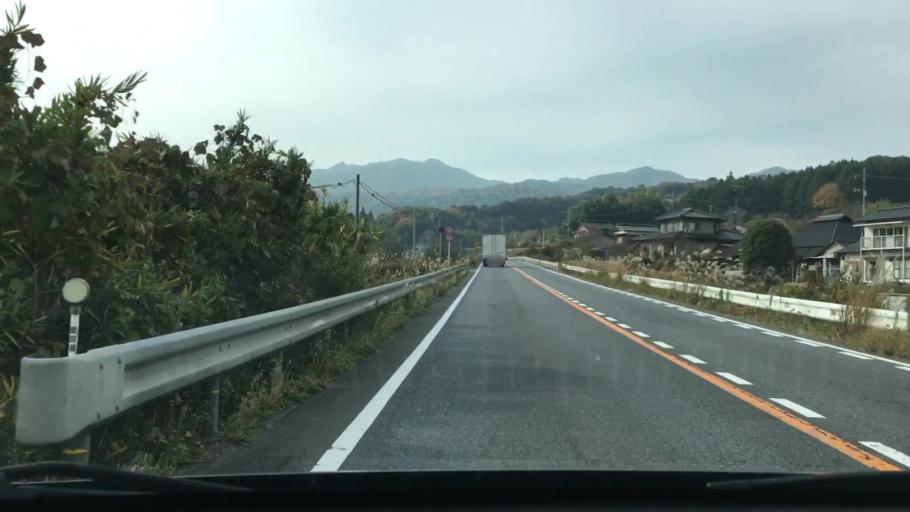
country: JP
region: Yamaguchi
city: Hikari
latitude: 34.0931
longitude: 132.0198
